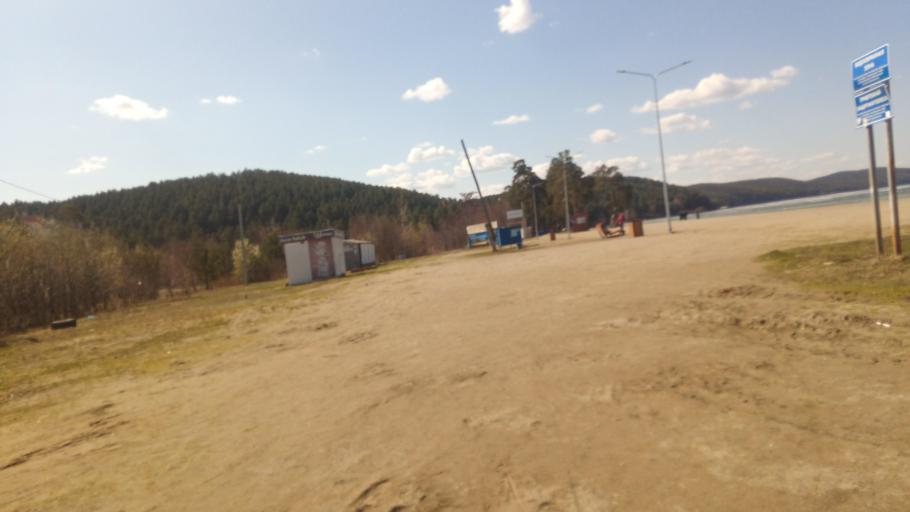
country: RU
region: Chelyabinsk
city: Turgoyak
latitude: 55.1536
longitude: 60.1104
